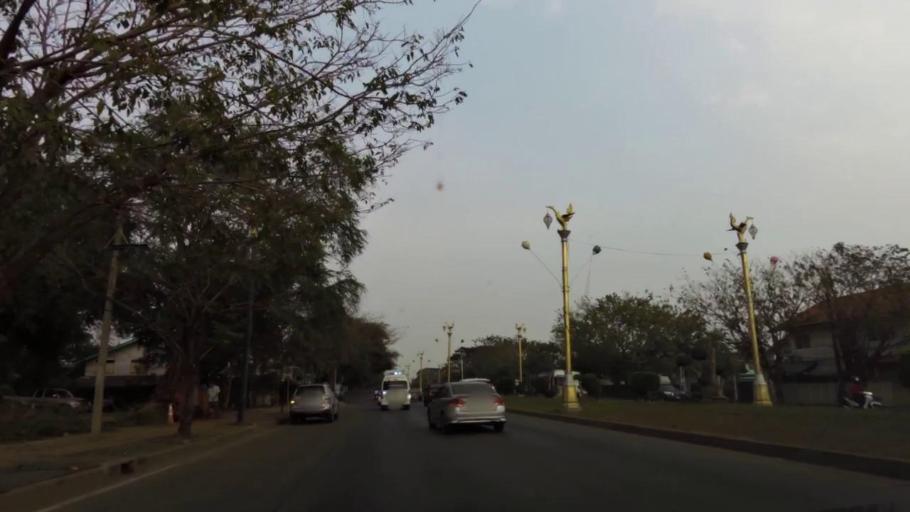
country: TH
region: Phra Nakhon Si Ayutthaya
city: Phra Nakhon Si Ayutthaya
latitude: 14.3510
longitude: 100.5695
